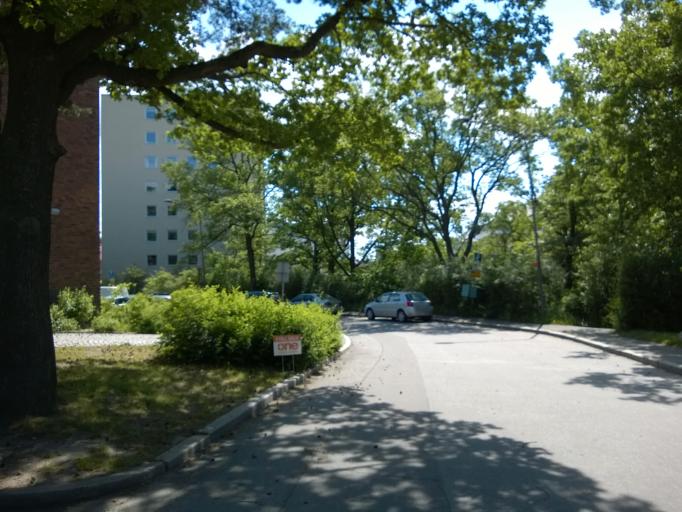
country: SE
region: Stockholm
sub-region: Solna Kommun
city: Solna
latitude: 59.3666
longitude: 17.9979
